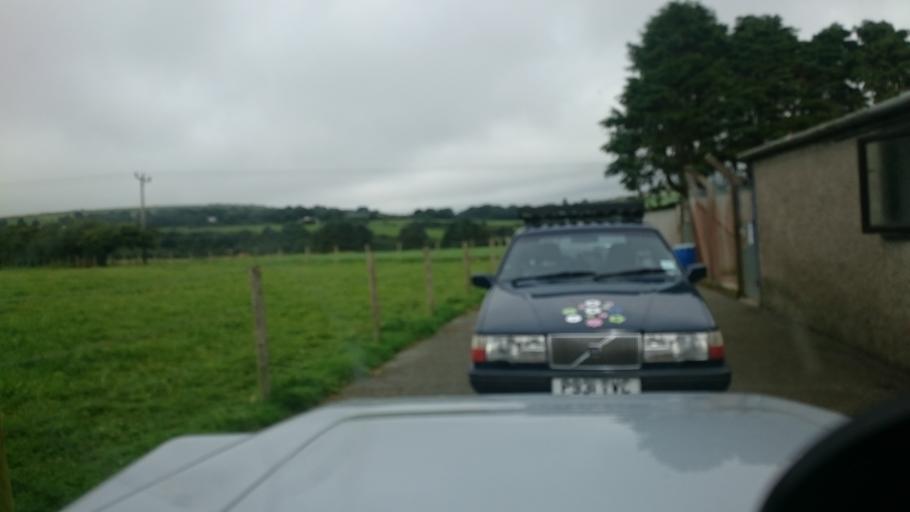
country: GB
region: Wales
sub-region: Pembrokeshire
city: Ambleston
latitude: 51.9250
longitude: -4.9384
